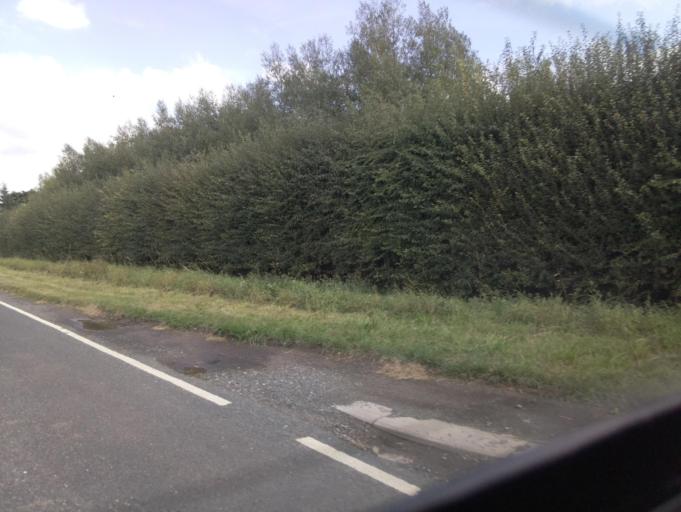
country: GB
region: England
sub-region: Darlington
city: High Coniscliffe
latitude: 54.4654
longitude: -1.6594
